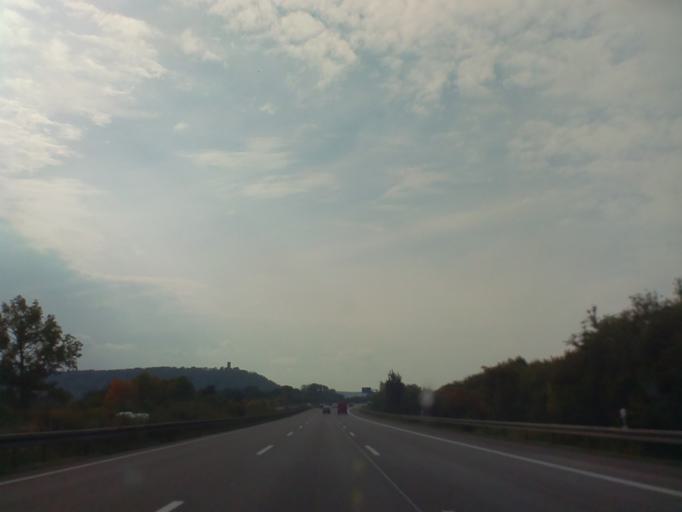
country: DE
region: Thuringia
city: Wandersleben
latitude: 50.8798
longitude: 10.8506
